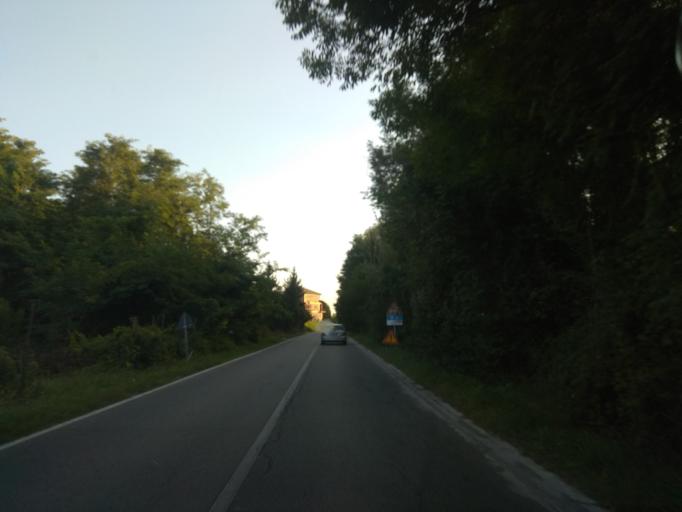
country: IT
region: Piedmont
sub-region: Provincia di Novara
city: Romagnano Sesia
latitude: 45.6403
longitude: 8.3865
